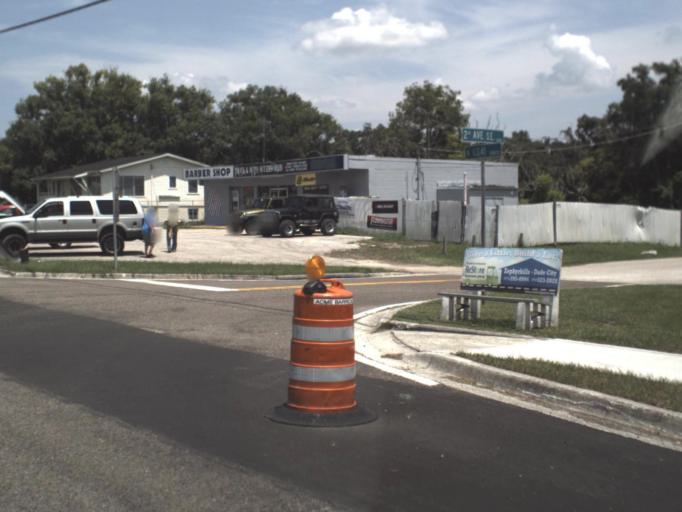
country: US
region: Florida
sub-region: Hillsborough County
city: Lutz
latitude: 28.1492
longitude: -82.4617
